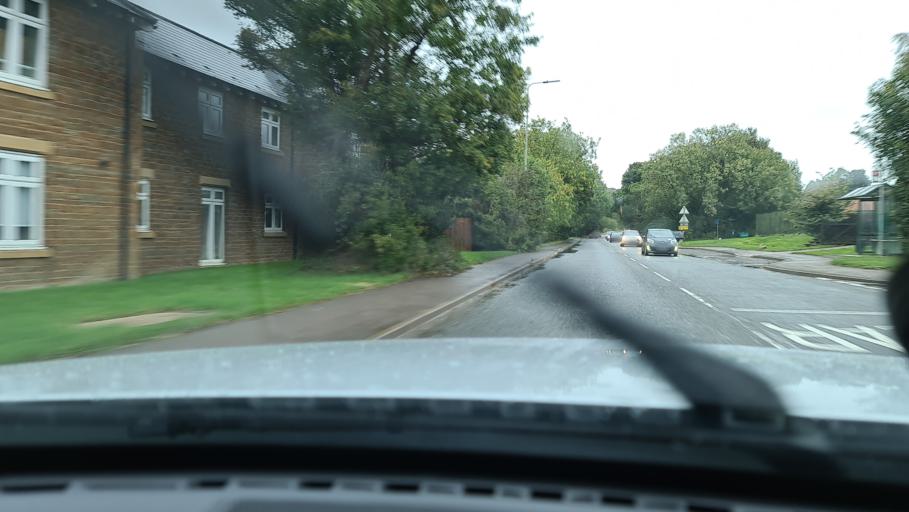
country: GB
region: England
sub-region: Oxfordshire
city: Adderbury
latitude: 52.0200
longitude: -1.3109
